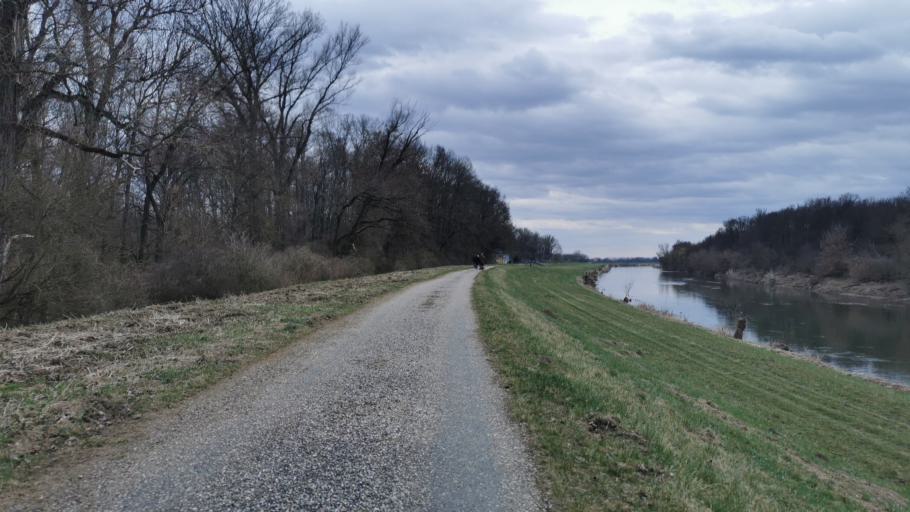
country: CZ
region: South Moravian
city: Hodonin
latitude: 48.8175
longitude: 17.1078
